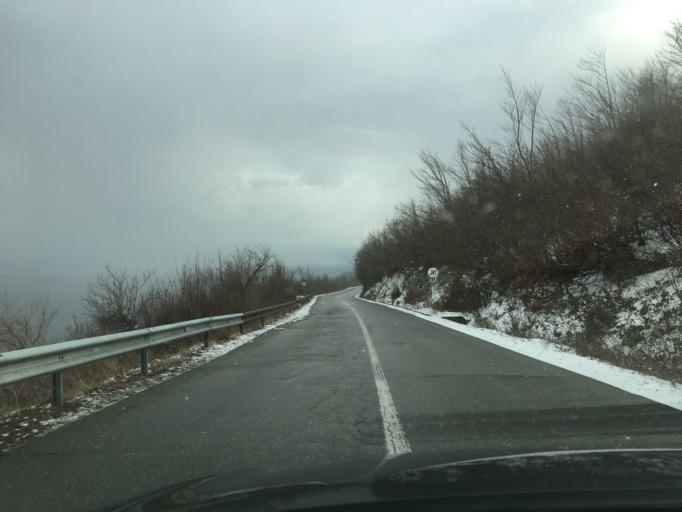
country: XK
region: Pec
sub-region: Komuna e Pejes
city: Dubova (Driloni)
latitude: 42.7583
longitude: 20.3007
